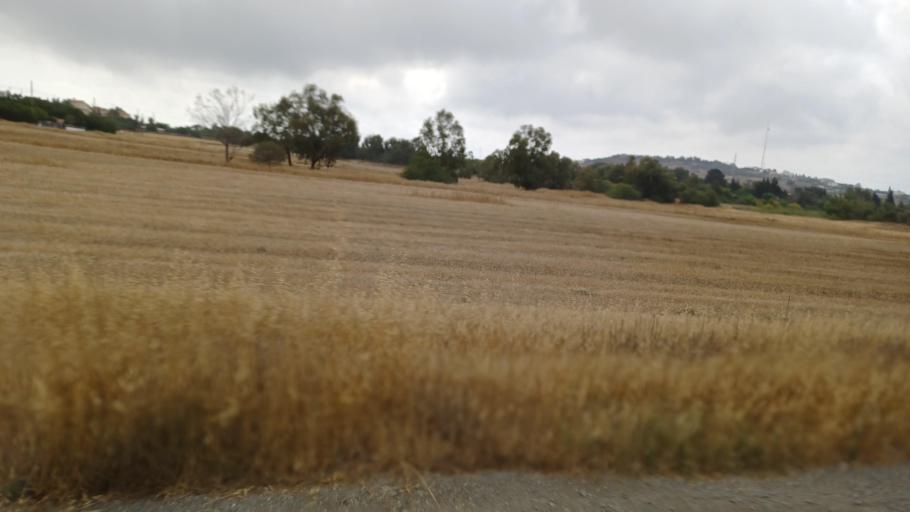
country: CY
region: Ammochostos
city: Protaras
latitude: 35.0171
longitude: 34.0199
